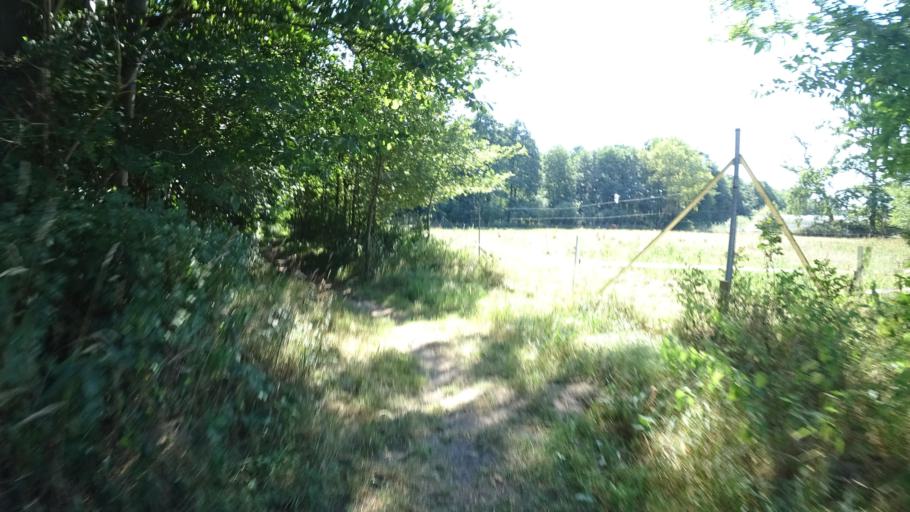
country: DE
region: North Rhine-Westphalia
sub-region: Regierungsbezirk Detmold
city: Steinhagen
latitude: 51.9500
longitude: 8.4654
